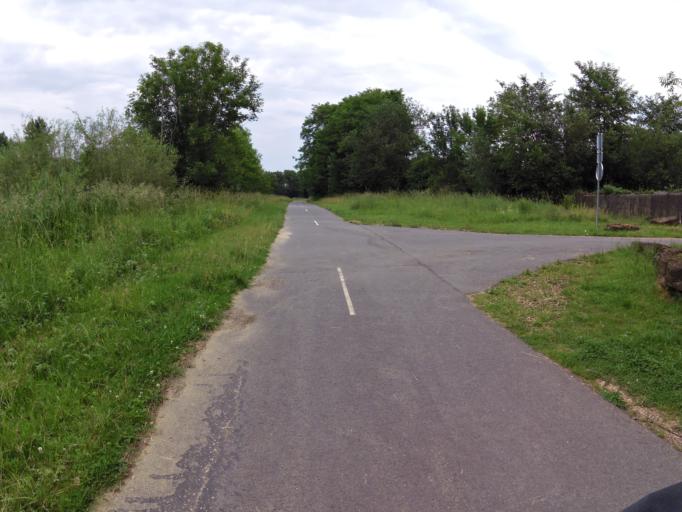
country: FR
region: Champagne-Ardenne
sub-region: Departement des Ardennes
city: Charleville-Mezieres
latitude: 49.7647
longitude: 4.7288
